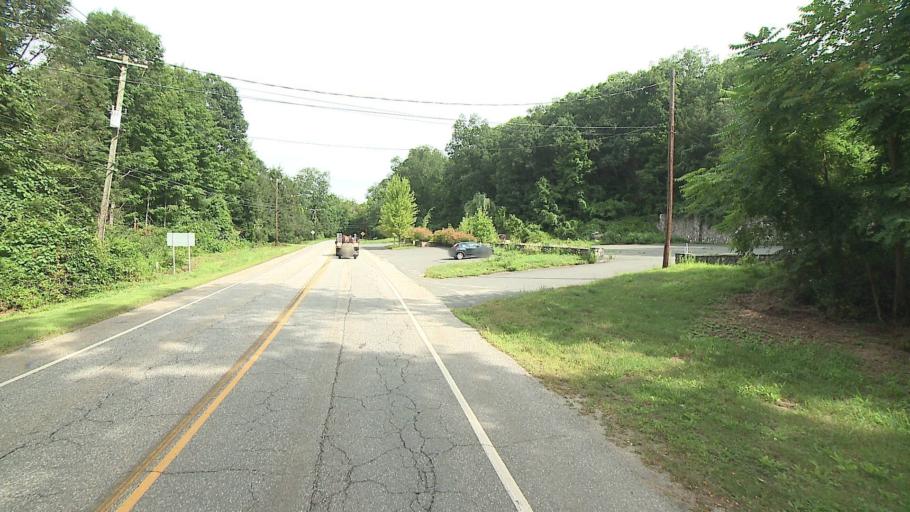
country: US
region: Connecticut
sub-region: Litchfield County
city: New Preston
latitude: 41.6446
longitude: -73.3167
